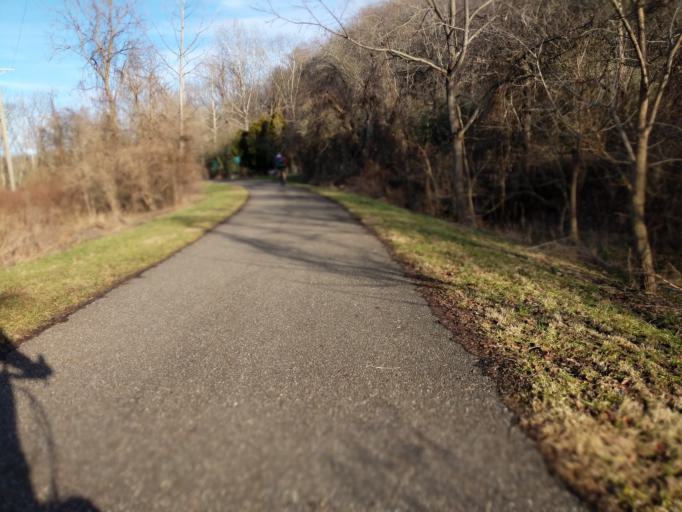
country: US
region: Ohio
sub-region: Athens County
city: Athens
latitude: 39.3399
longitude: -82.1109
